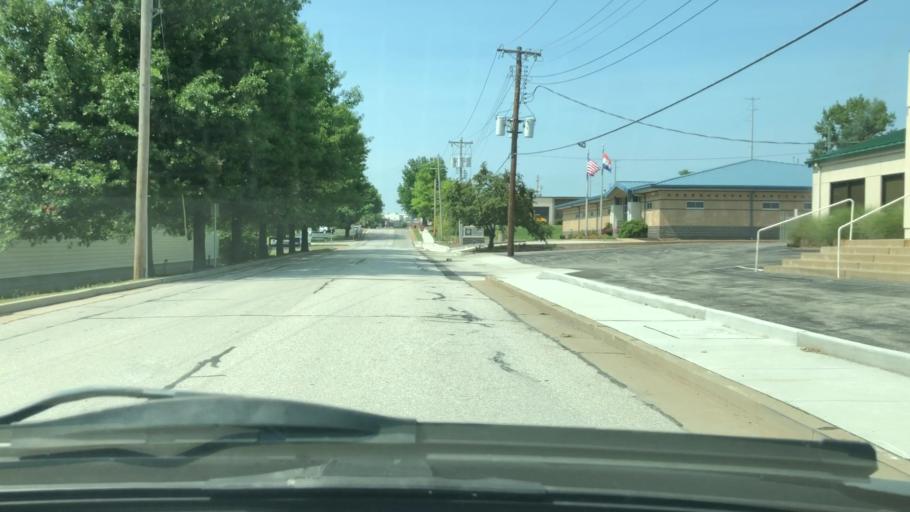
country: US
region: Missouri
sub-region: Saint Louis County
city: Brentwood
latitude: 38.6202
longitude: -90.3365
